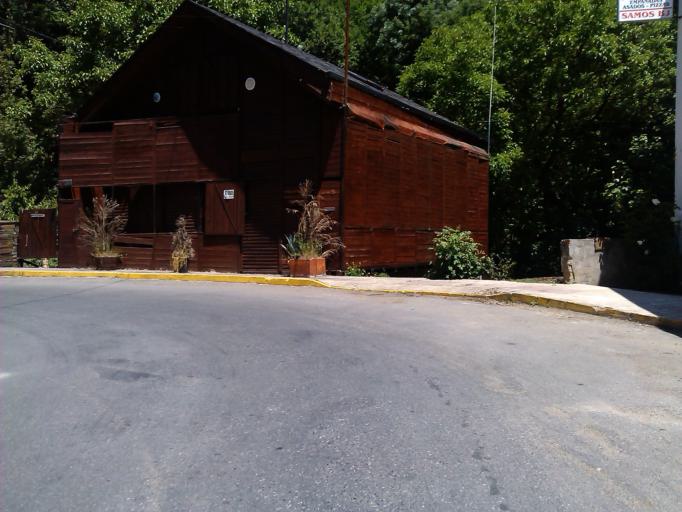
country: ES
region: Galicia
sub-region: Provincia de Lugo
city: Samos
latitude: 42.7330
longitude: -7.3244
